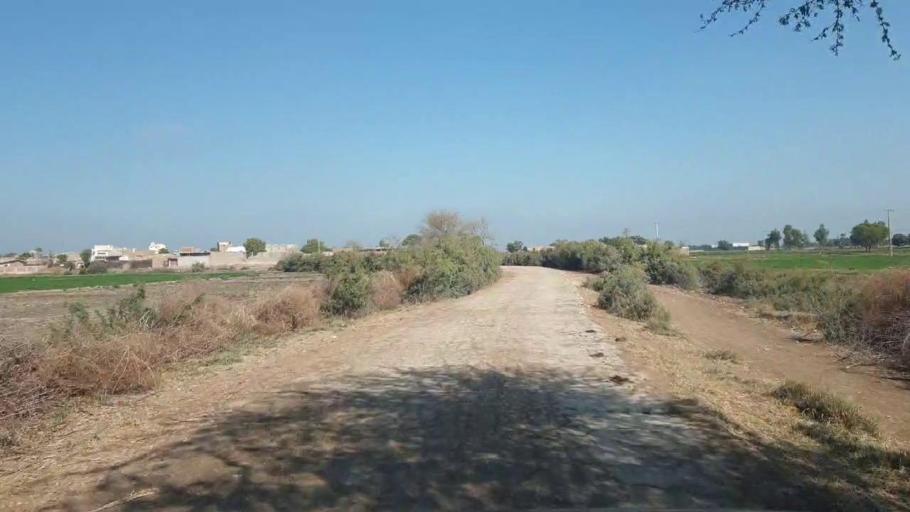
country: PK
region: Sindh
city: Bhit Shah
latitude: 25.8824
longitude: 68.5262
